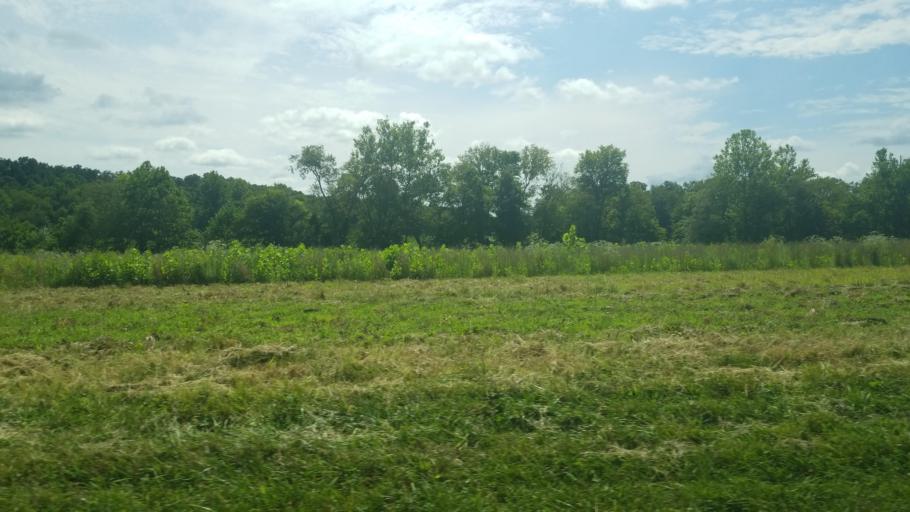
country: US
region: Illinois
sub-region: Saline County
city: Carrier Mills
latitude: 37.7976
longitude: -88.7469
